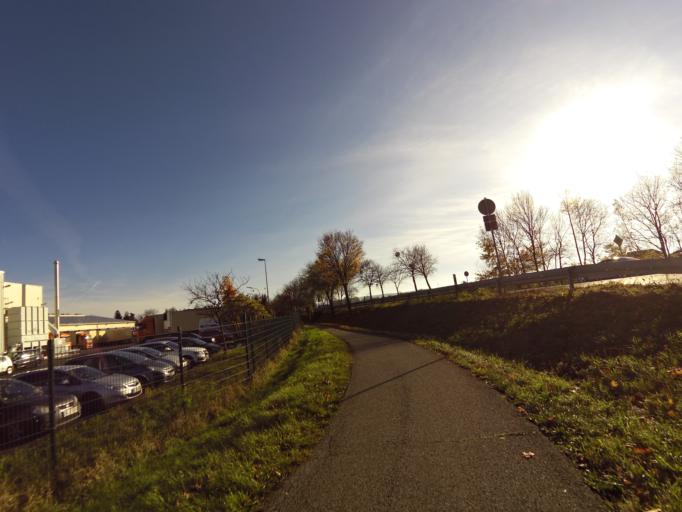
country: DE
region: North Rhine-Westphalia
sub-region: Regierungsbezirk Koln
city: Euskirchen
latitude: 50.6476
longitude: 6.8187
